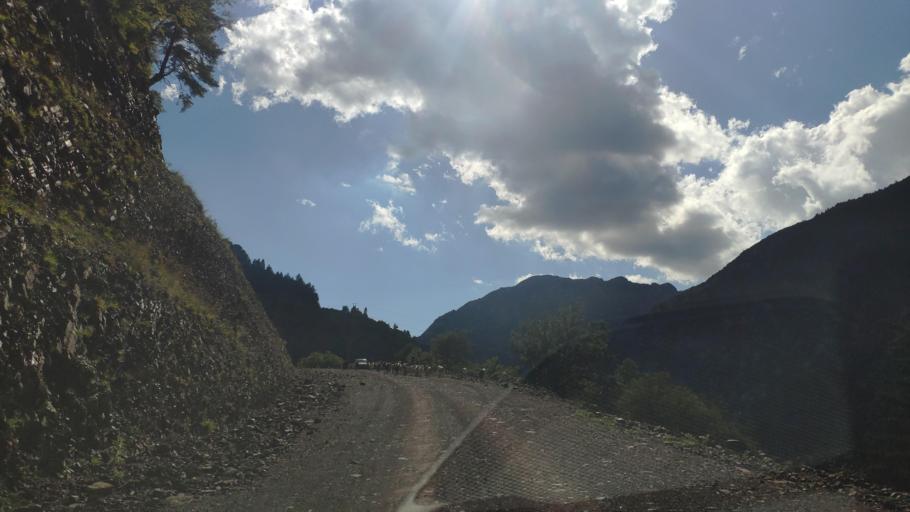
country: GR
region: Central Greece
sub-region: Nomos Evrytanias
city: Kerasochori
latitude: 39.1206
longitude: 21.6263
